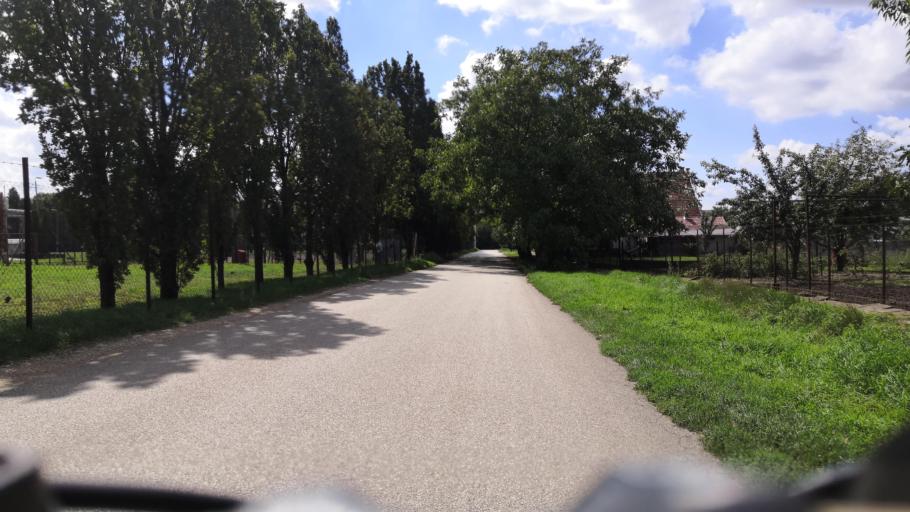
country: HU
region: Csongrad
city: Szeged
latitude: 46.2794
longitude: 20.1286
